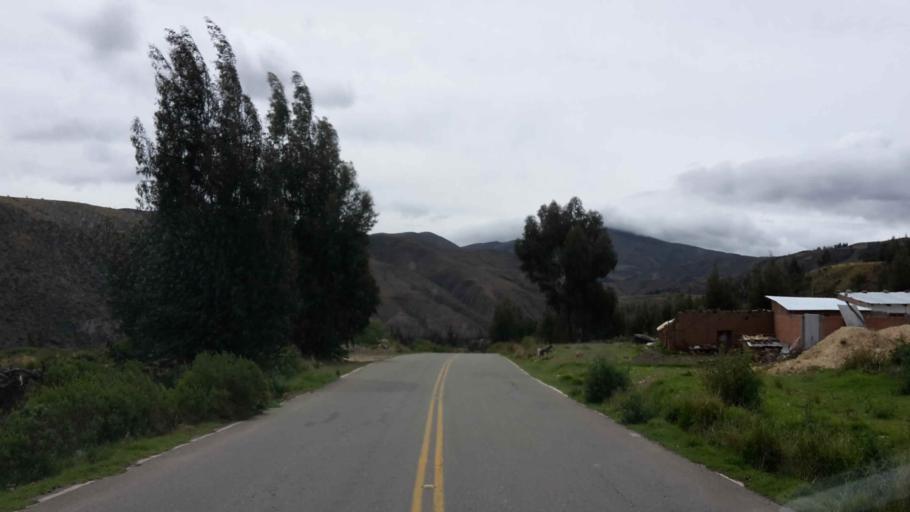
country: BO
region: Cochabamba
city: Colomi
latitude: -17.4137
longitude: -65.7671
